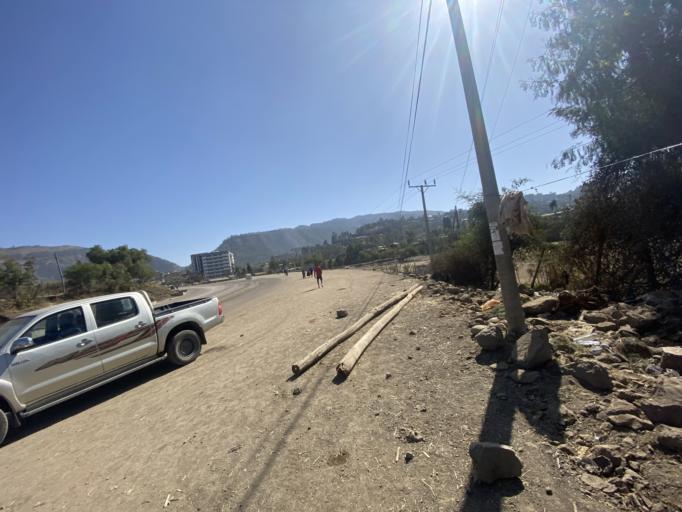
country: ET
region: Amhara
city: Robit
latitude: 11.8247
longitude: 39.5908
